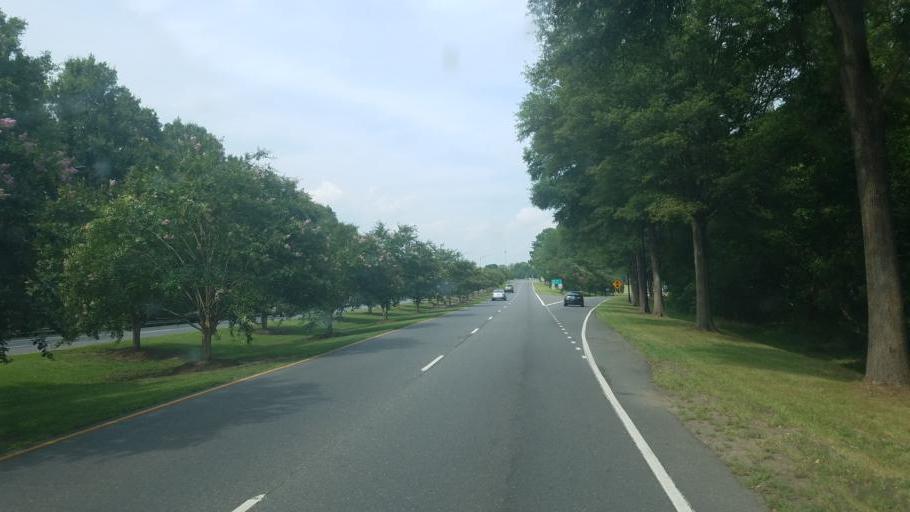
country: US
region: South Carolina
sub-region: York County
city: Rock Hill
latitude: 34.9363
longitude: -80.9999
